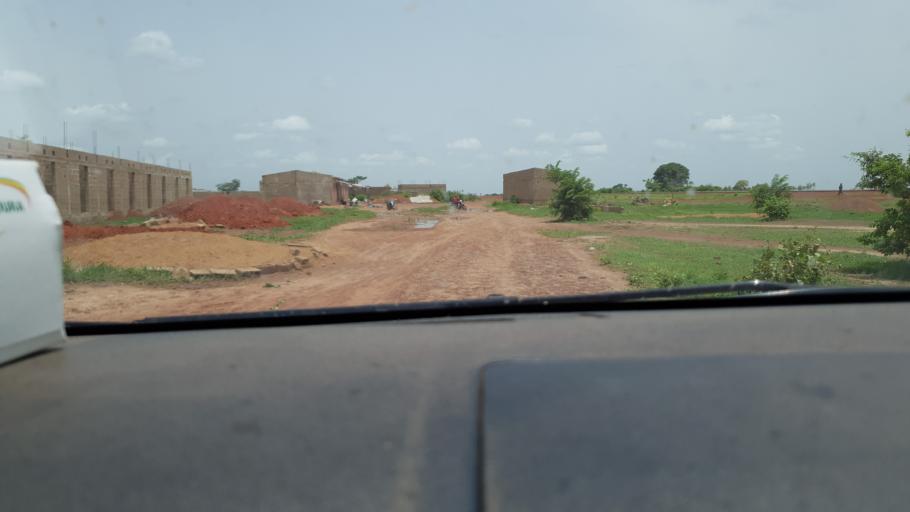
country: ML
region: Koulikoro
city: Koulikoro
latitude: 12.7116
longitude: -7.4237
